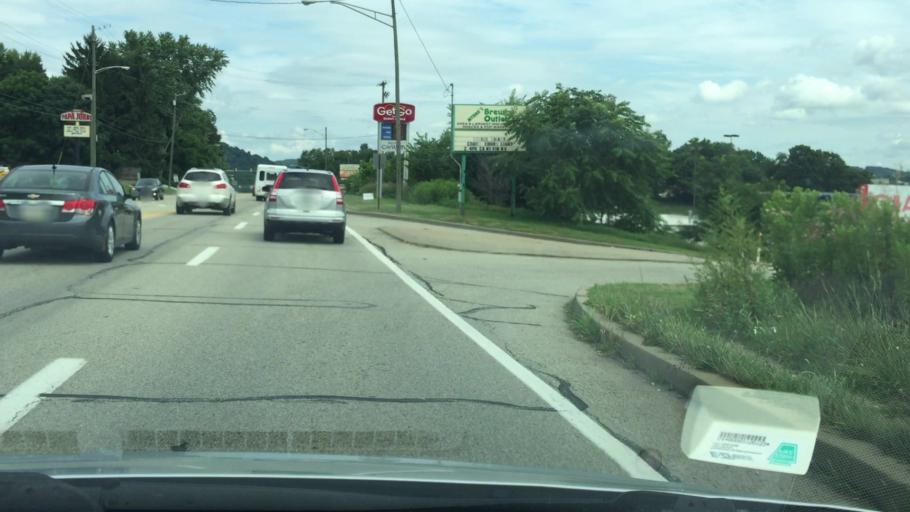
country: US
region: Pennsylvania
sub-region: Allegheny County
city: Tarentum
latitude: 40.5909
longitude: -79.7512
